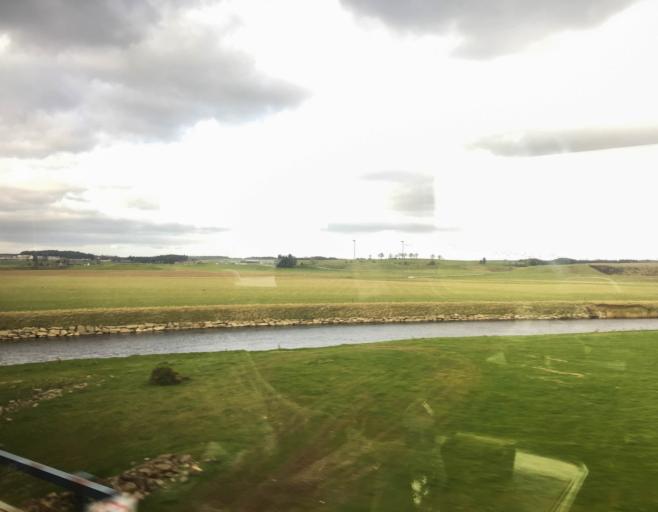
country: GB
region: Scotland
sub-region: South Lanarkshire
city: Carnwath
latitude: 55.6799
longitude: -3.6512
